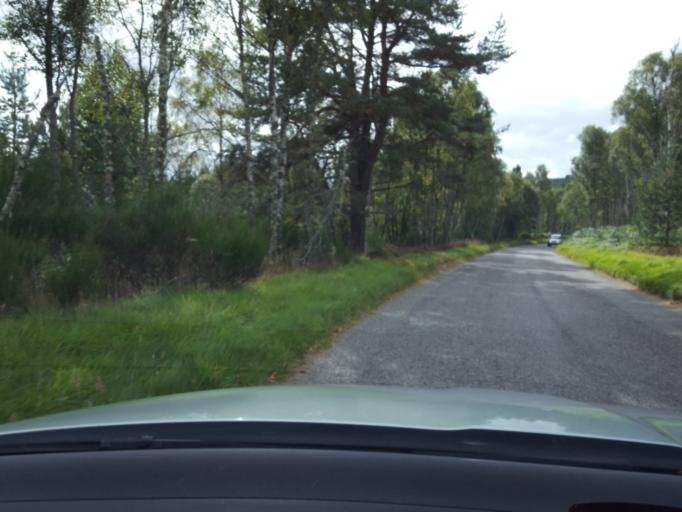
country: GB
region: Scotland
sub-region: Aberdeenshire
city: Ballater
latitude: 57.0781
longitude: -2.9397
